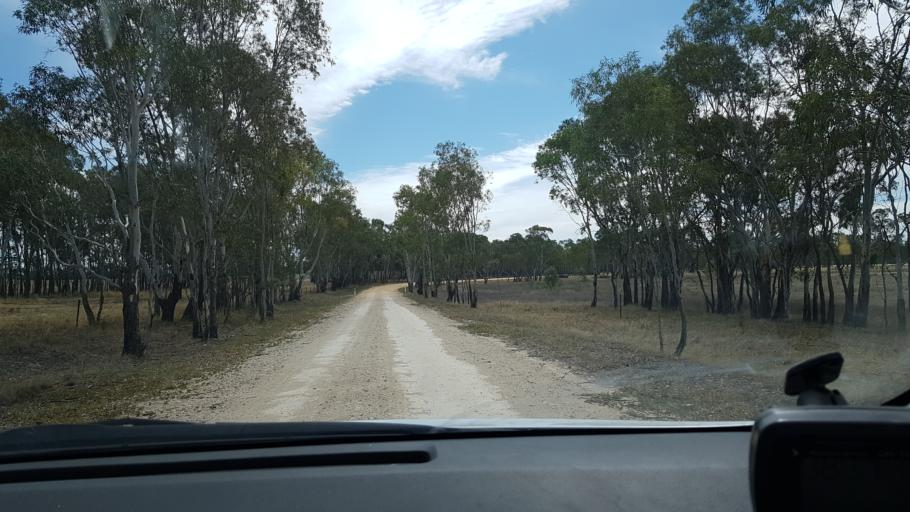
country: AU
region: Victoria
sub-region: Horsham
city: Horsham
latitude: -36.6872
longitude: 141.7810
